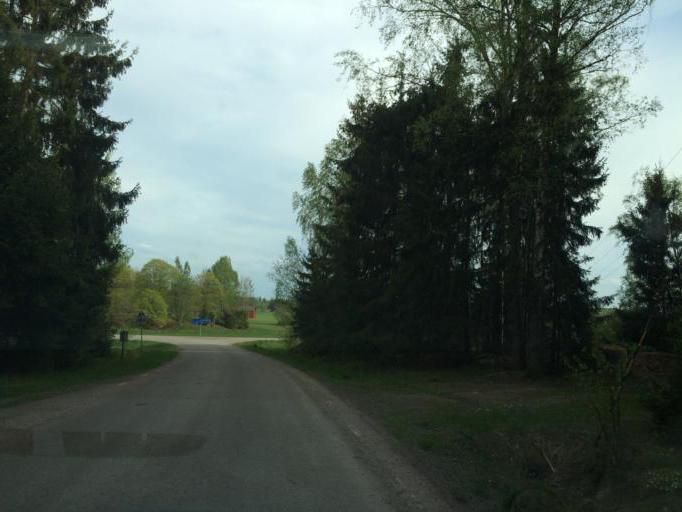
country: SE
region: Vaestmanland
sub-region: Hallstahammars Kommun
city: Hallstahammar
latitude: 59.6011
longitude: 16.1003
